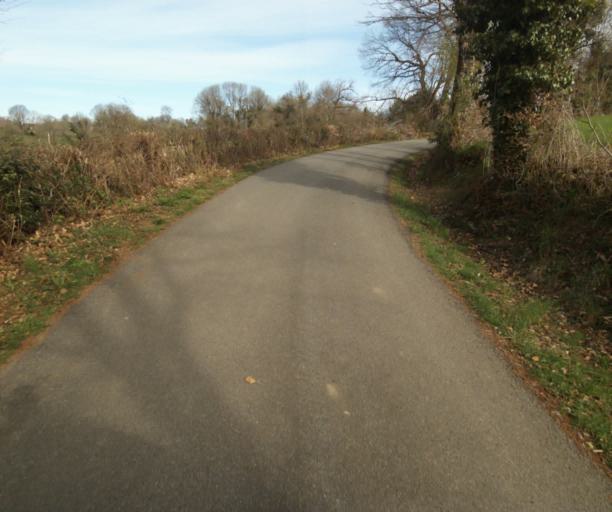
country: FR
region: Limousin
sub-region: Departement de la Correze
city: Chamboulive
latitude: 45.4196
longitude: 1.7891
